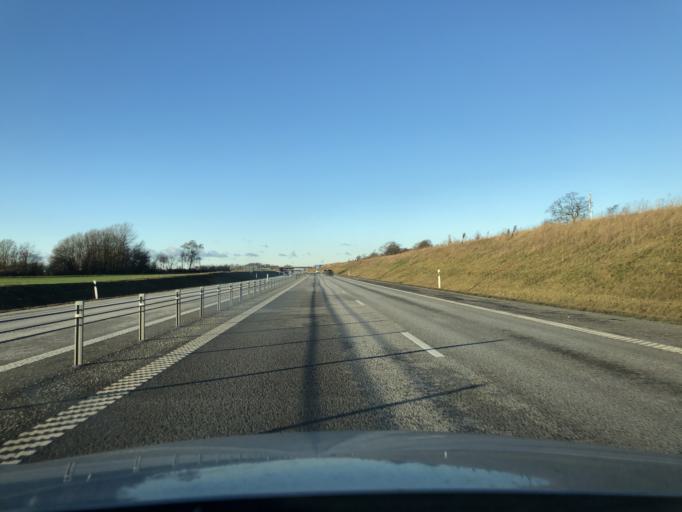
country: SE
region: Skane
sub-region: Trelleborgs Kommun
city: Skare
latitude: 55.4300
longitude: 13.0480
